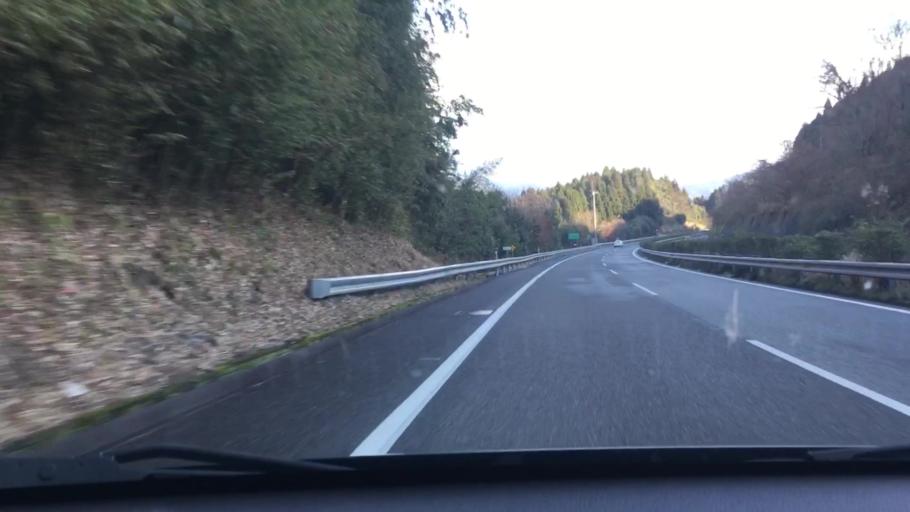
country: JP
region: Kumamoto
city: Hitoyoshi
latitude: 32.1789
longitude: 130.7866
